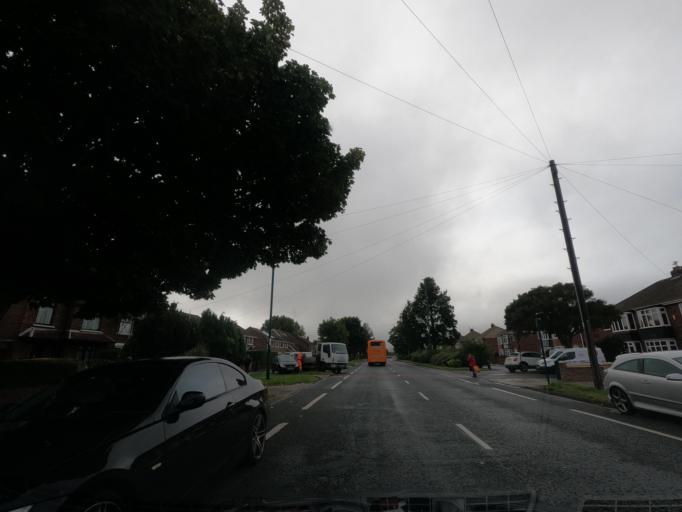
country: GB
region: England
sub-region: Redcar and Cleveland
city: Redcar
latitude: 54.6082
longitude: -1.0836
